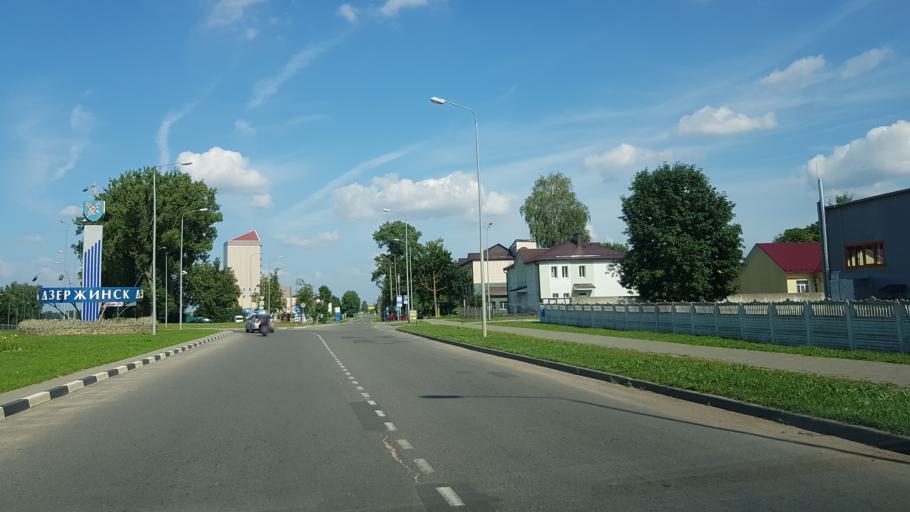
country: BY
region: Minsk
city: Dzyarzhynsk
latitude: 53.6866
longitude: 27.1513
